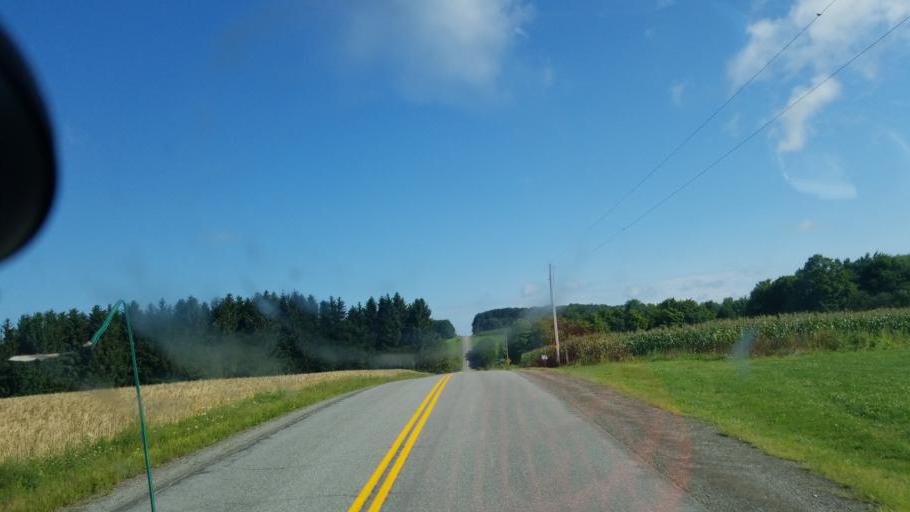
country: US
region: New York
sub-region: Allegany County
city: Andover
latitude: 42.1554
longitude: -77.7136
